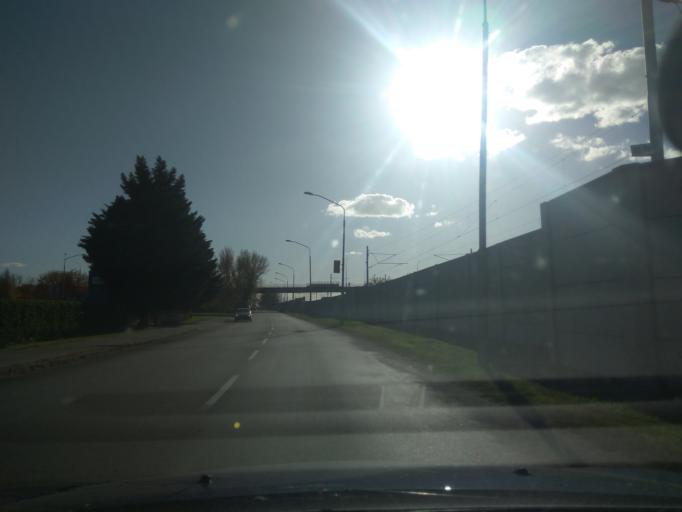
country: SK
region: Trnavsky
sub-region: Okres Trnava
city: Piestany
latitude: 48.5905
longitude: 17.8109
